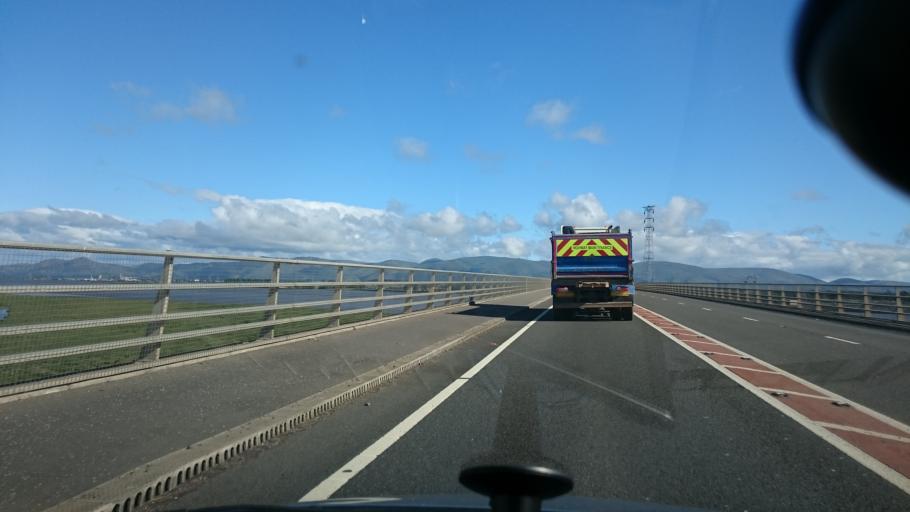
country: GB
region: Scotland
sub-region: Fife
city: Kincardine
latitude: 56.0655
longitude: -3.7360
